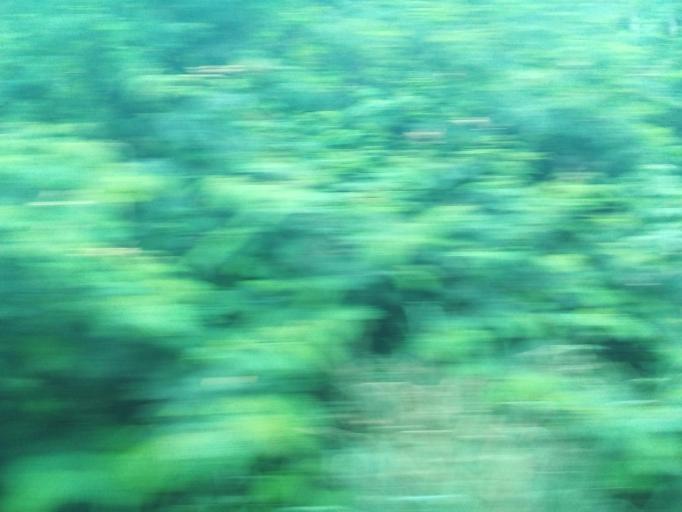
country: BR
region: Minas Gerais
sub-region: Joao Monlevade
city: Joao Monlevade
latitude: -19.8251
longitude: -43.1086
